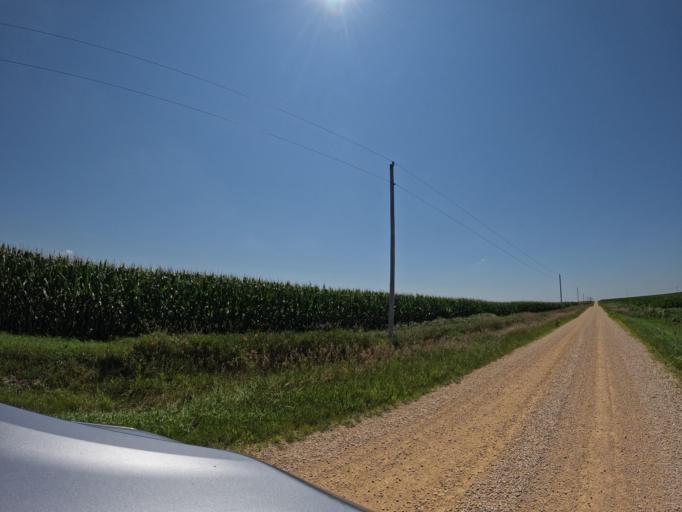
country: US
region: Iowa
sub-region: Clinton County
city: Camanche
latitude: 41.7907
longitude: -90.3937
